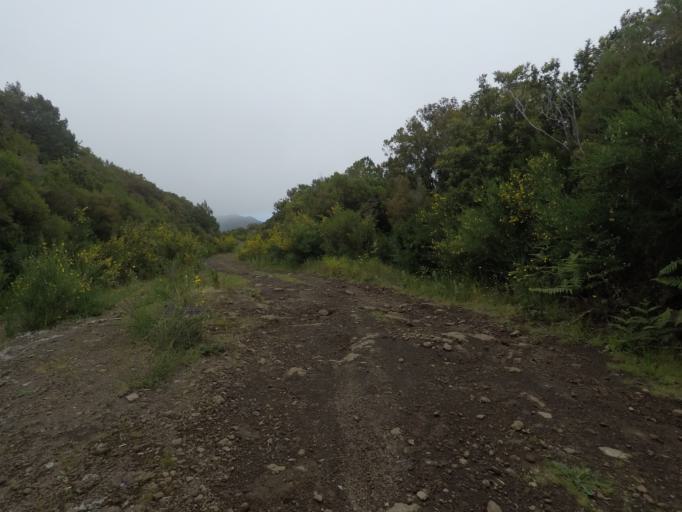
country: PT
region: Madeira
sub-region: Sao Vicente
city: Sao Vicente
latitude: 32.7710
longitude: -17.0562
